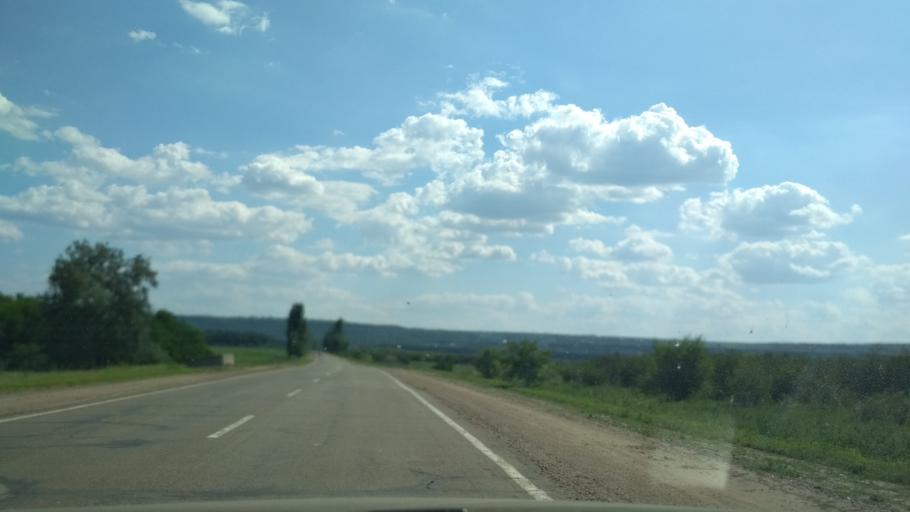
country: MD
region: Chisinau
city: Vadul lui Voda
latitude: 47.1125
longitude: 29.1041
